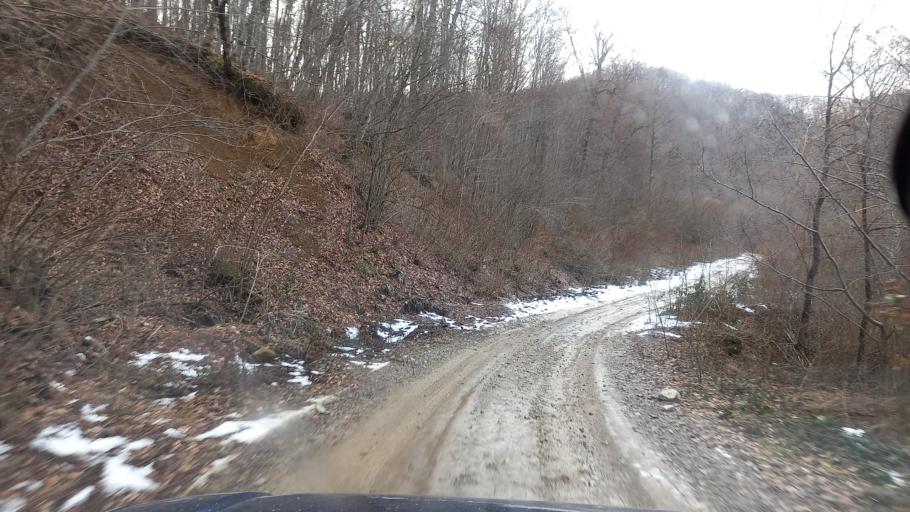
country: RU
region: Adygeya
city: Kamennomostskiy
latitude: 44.1644
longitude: 40.3008
